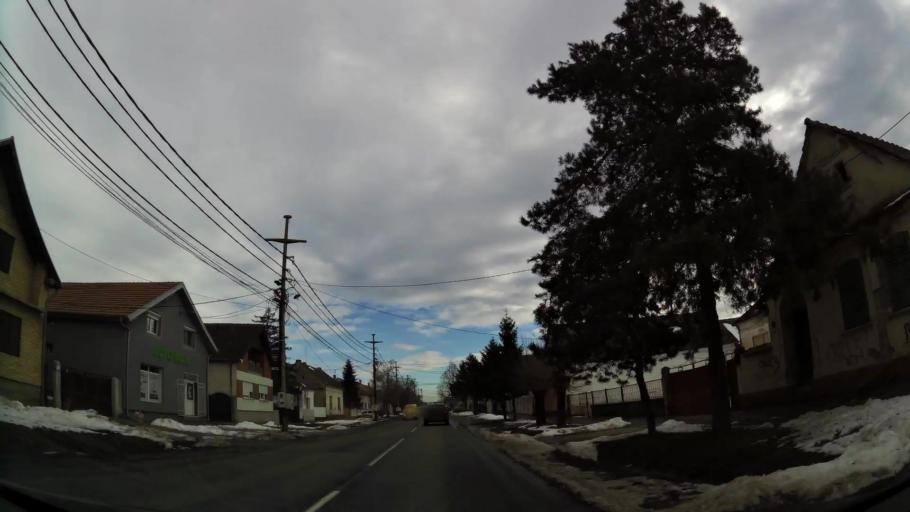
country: RS
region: Central Serbia
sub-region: Belgrade
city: Surcin
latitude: 44.7897
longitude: 20.2633
